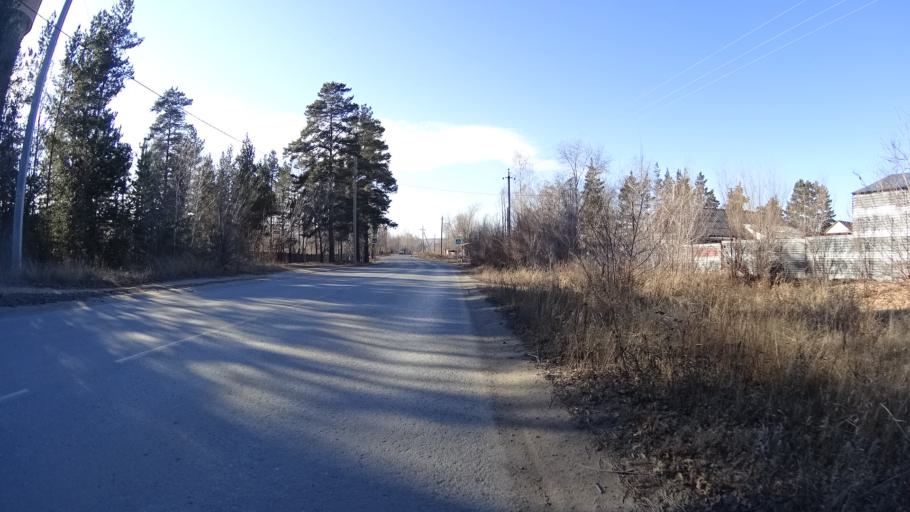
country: RU
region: Chelyabinsk
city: Troitsk
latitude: 54.0507
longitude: 61.6308
